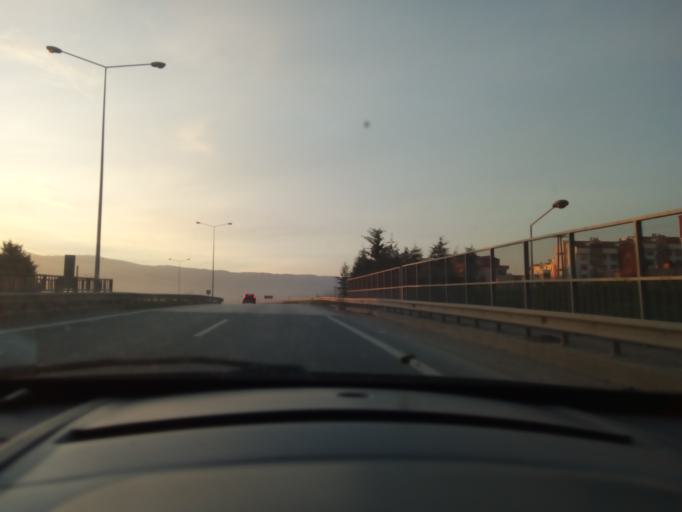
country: TR
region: Bursa
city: Niluefer
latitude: 40.2625
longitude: 28.9434
